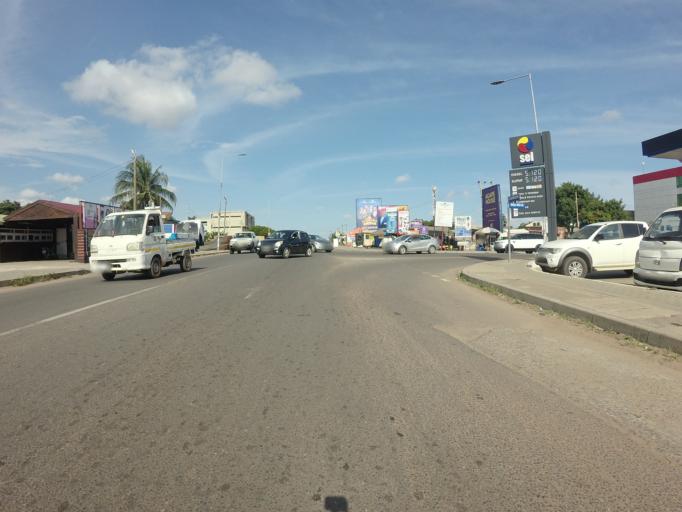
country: GH
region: Greater Accra
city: Medina Estates
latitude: 5.6424
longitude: -0.1625
